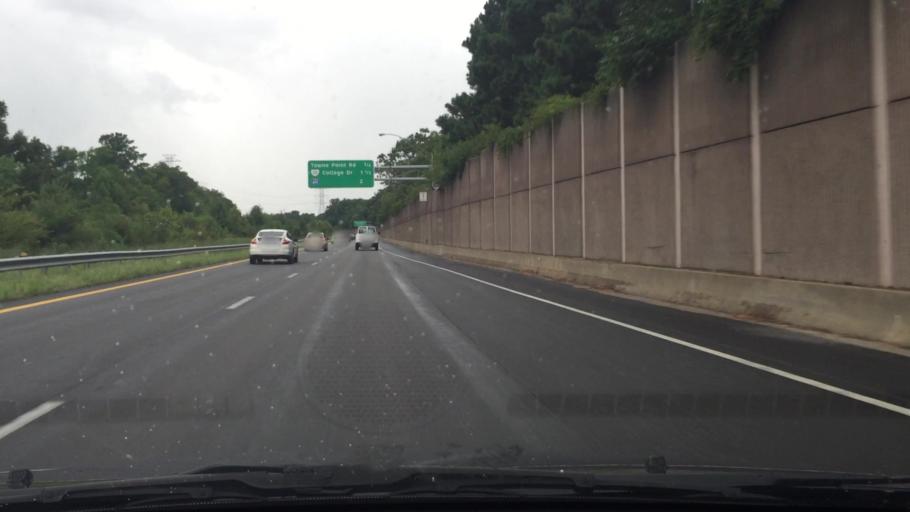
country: US
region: Virginia
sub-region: City of Portsmouth
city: Portsmouth Heights
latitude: 36.8730
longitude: -76.3853
